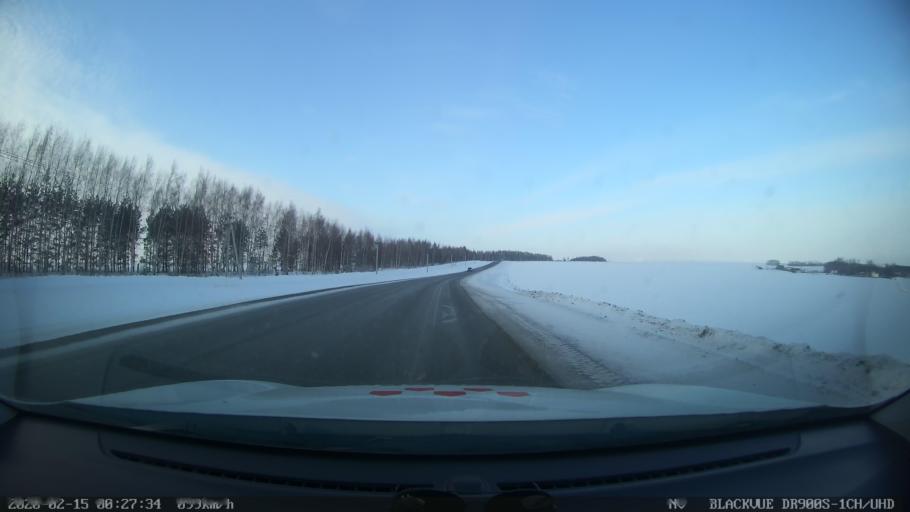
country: RU
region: Tatarstan
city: Verkhniy Uslon
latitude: 55.6299
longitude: 48.8732
